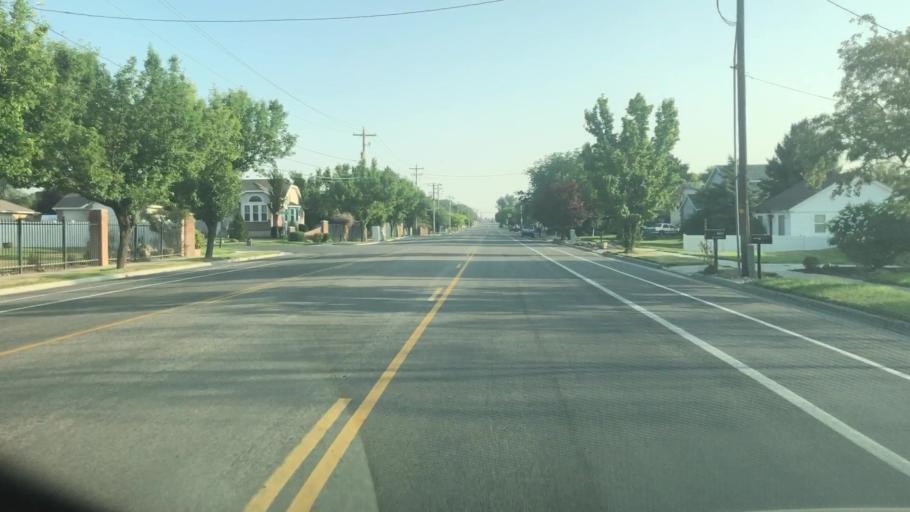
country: US
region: Utah
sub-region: Salt Lake County
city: South Jordan
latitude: 40.5541
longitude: -111.9292
